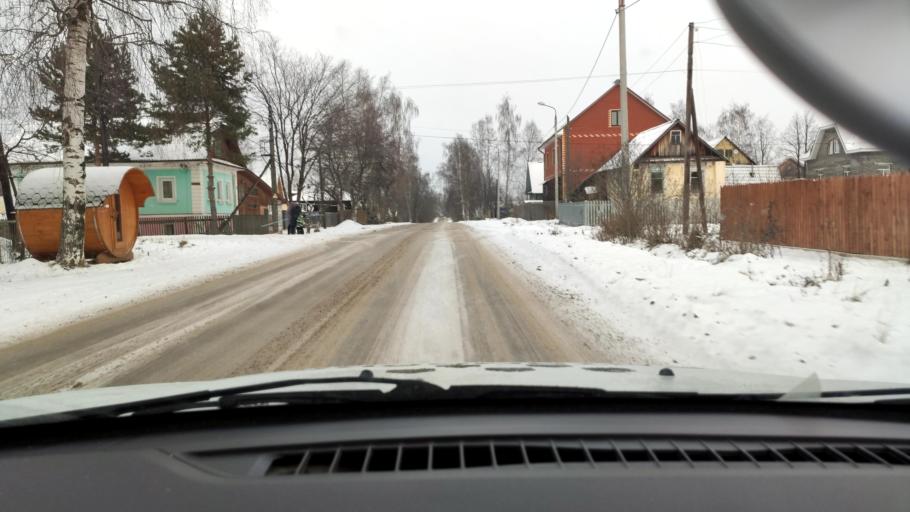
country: RU
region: Perm
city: Polazna
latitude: 58.1186
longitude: 56.3944
